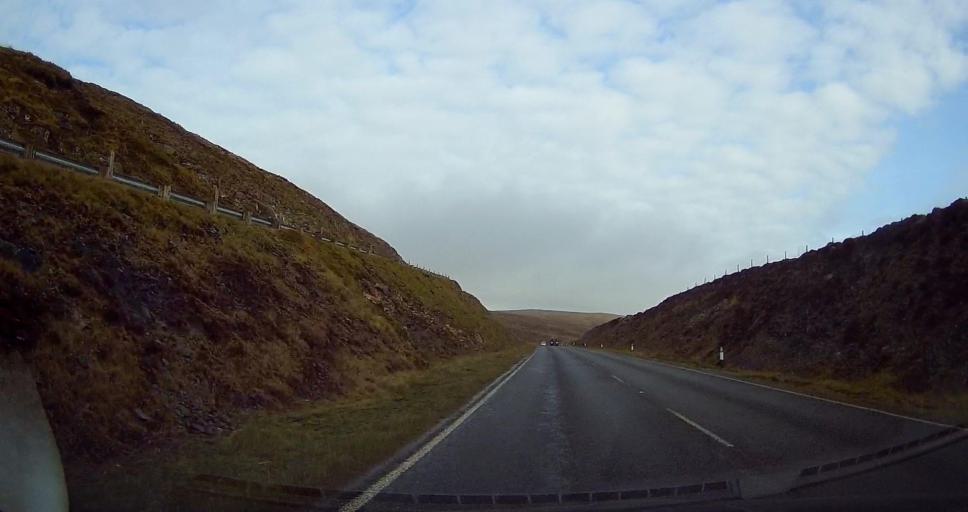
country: GB
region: Scotland
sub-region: Shetland Islands
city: Sandwick
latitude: 60.0671
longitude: -1.2250
